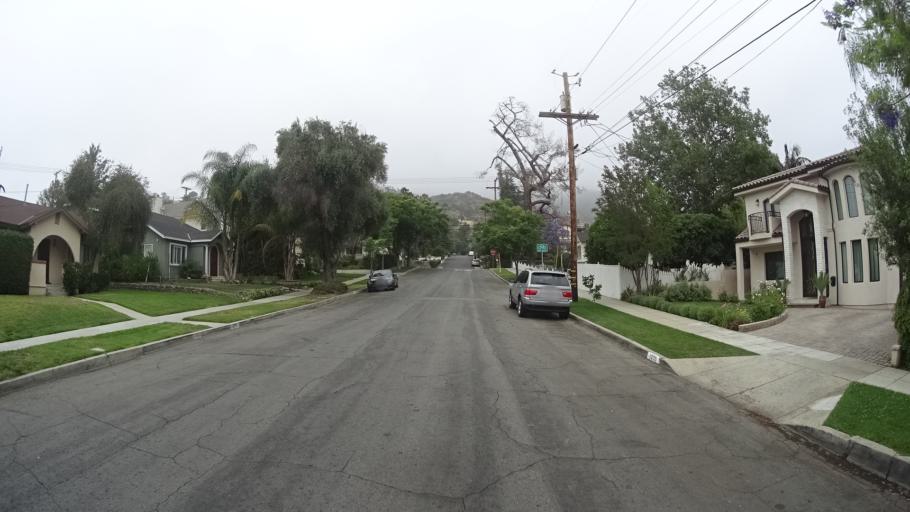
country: US
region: California
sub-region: Los Angeles County
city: Burbank
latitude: 34.1883
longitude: -118.2922
